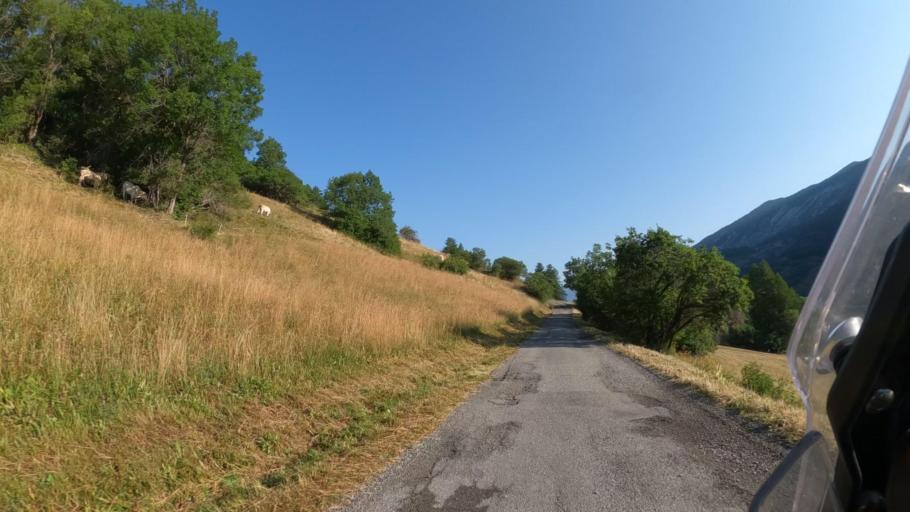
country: FR
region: Provence-Alpes-Cote d'Azur
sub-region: Departement des Hautes-Alpes
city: Guillestre
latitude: 44.6056
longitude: 6.6841
